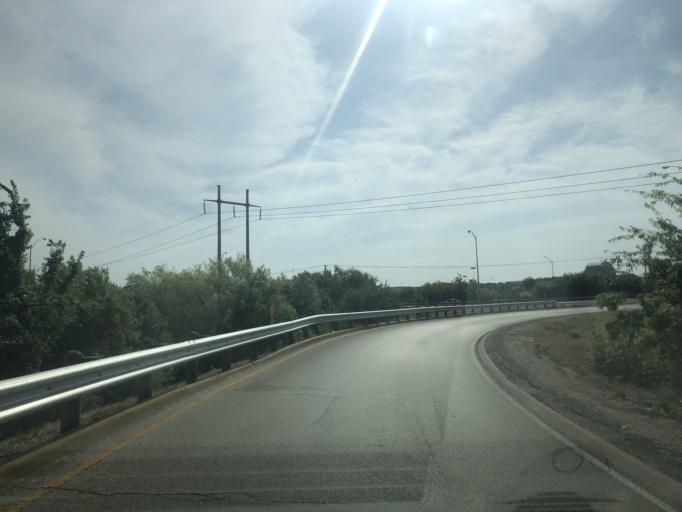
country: US
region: Texas
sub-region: Tarrant County
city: White Settlement
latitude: 32.7385
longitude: -97.4421
